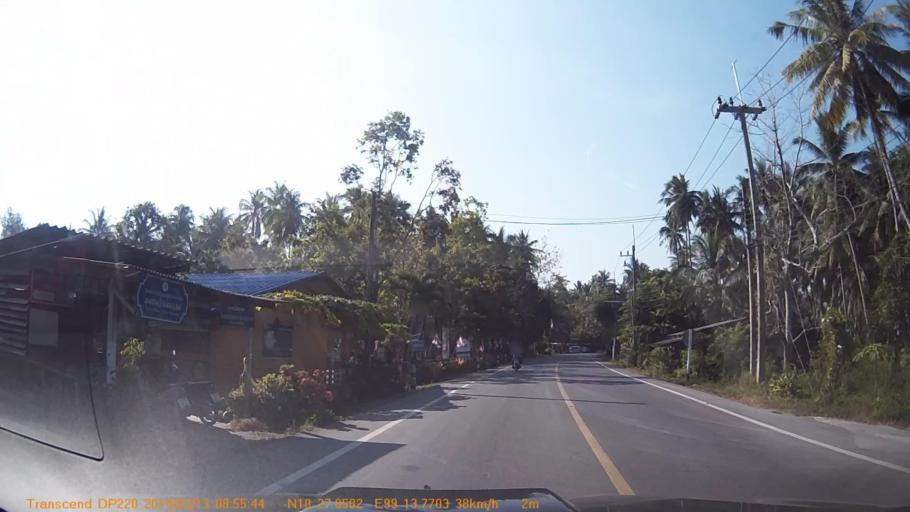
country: TH
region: Chumphon
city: Chumphon
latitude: 10.4643
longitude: 99.2295
